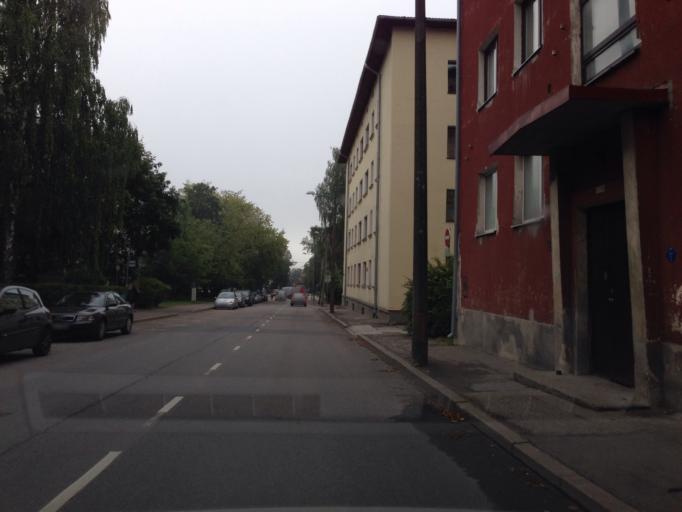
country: EE
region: Tartu
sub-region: Tartu linn
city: Tartu
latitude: 58.3758
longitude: 26.7177
